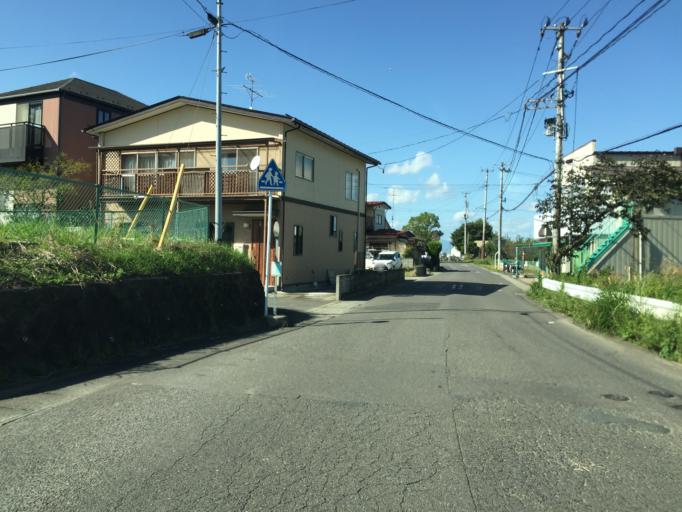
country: JP
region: Fukushima
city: Sukagawa
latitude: 37.2741
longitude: 140.3788
